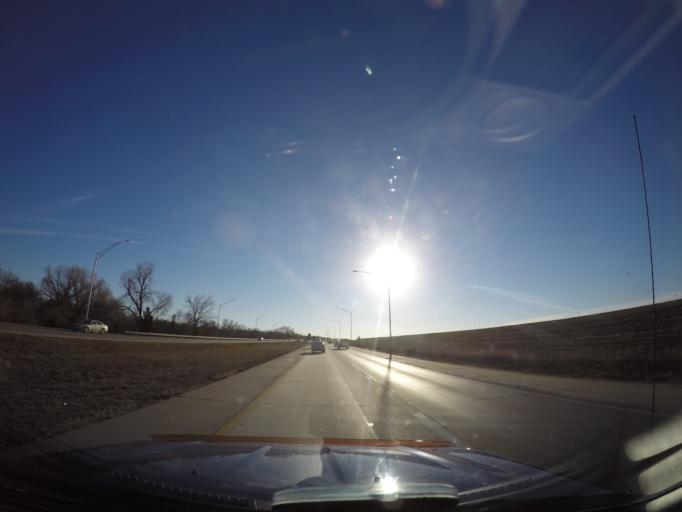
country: US
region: Kansas
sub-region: Sedgwick County
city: Wichita
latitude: 37.7277
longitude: -97.3845
